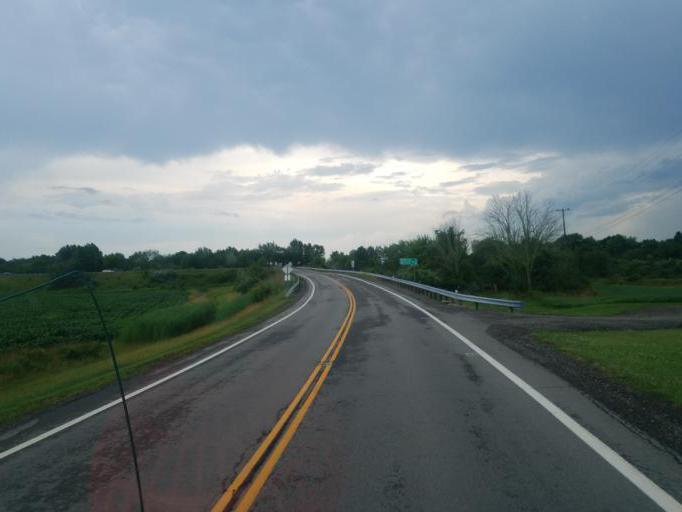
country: US
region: Ohio
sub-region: Wayne County
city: Doylestown
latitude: 40.9575
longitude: -81.7380
